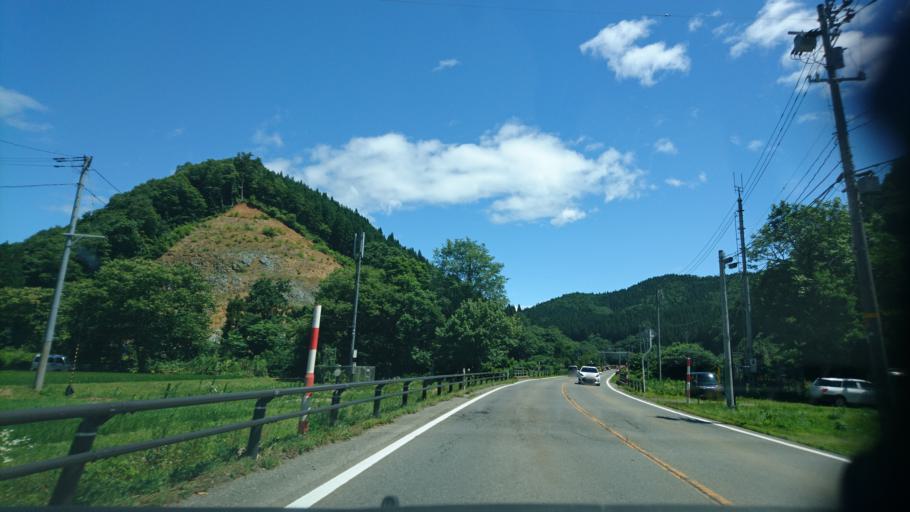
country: JP
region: Akita
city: Kakunodatemachi
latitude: 39.6511
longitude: 140.6677
